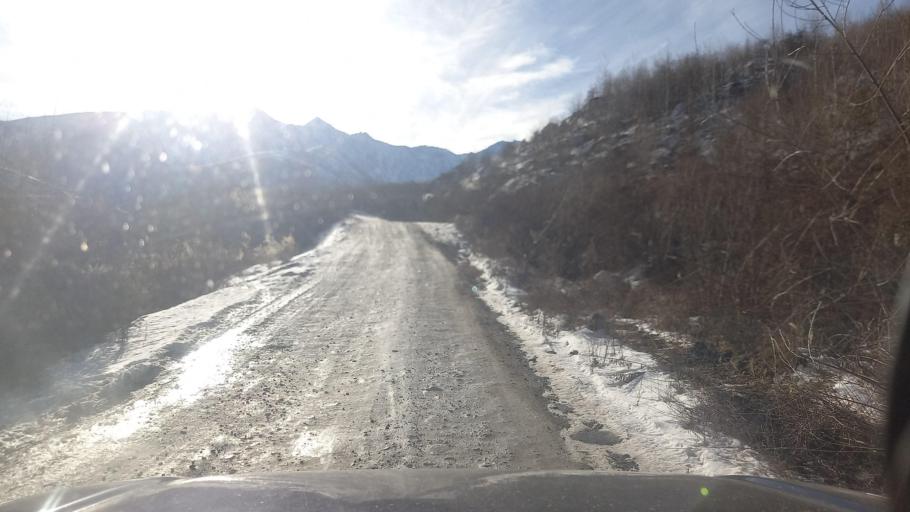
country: RU
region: Ingushetiya
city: Dzhayrakh
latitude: 42.8603
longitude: 44.5196
